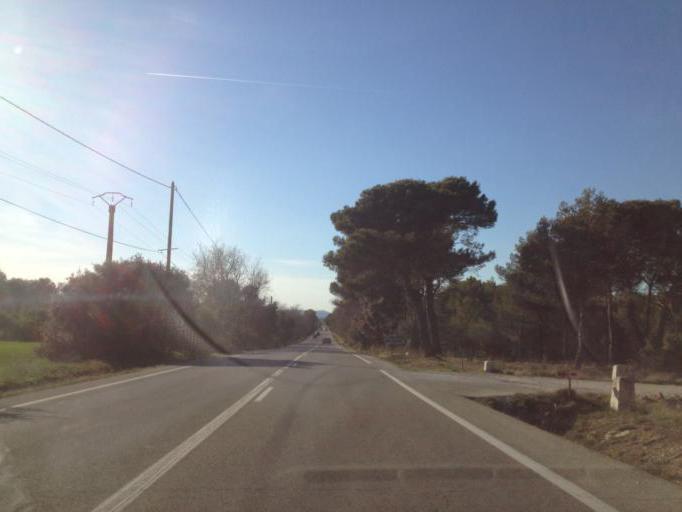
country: FR
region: Provence-Alpes-Cote d'Azur
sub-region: Departement des Bouches-du-Rhone
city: Eguilles
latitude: 43.6044
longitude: 5.3390
